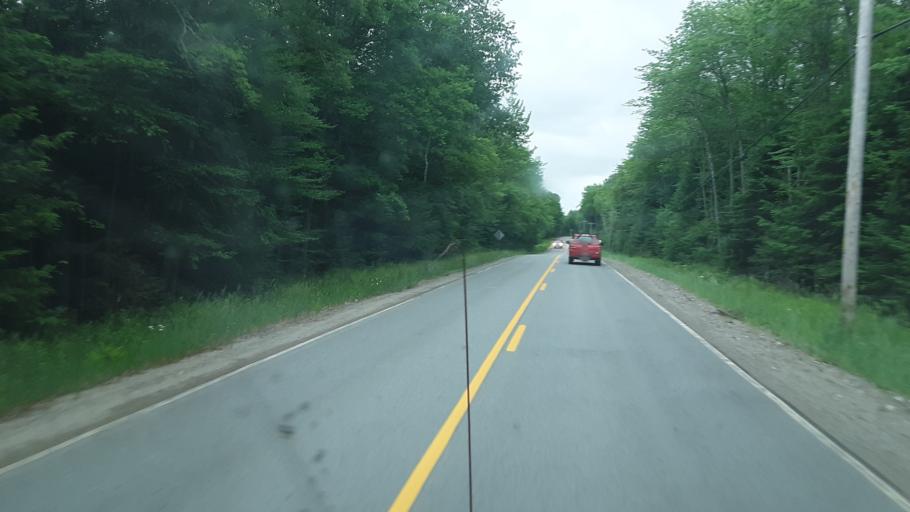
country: US
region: Maine
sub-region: Penobscot County
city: Millinocket
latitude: 45.6801
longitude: -68.7452
